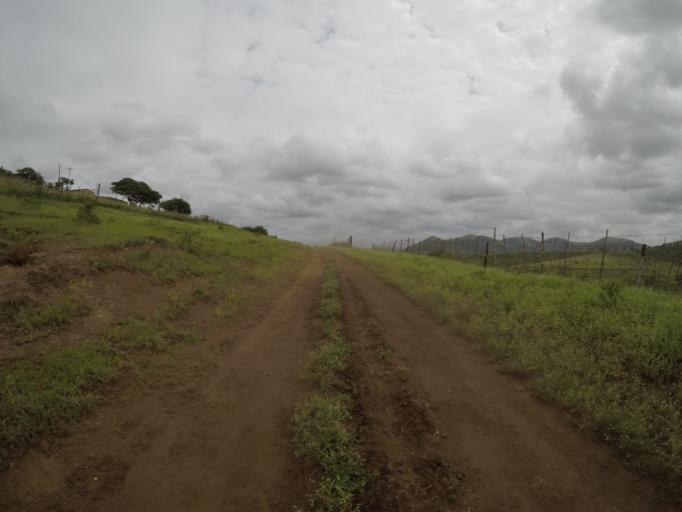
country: ZA
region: KwaZulu-Natal
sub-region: uThungulu District Municipality
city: Empangeni
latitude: -28.6166
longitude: 31.8915
